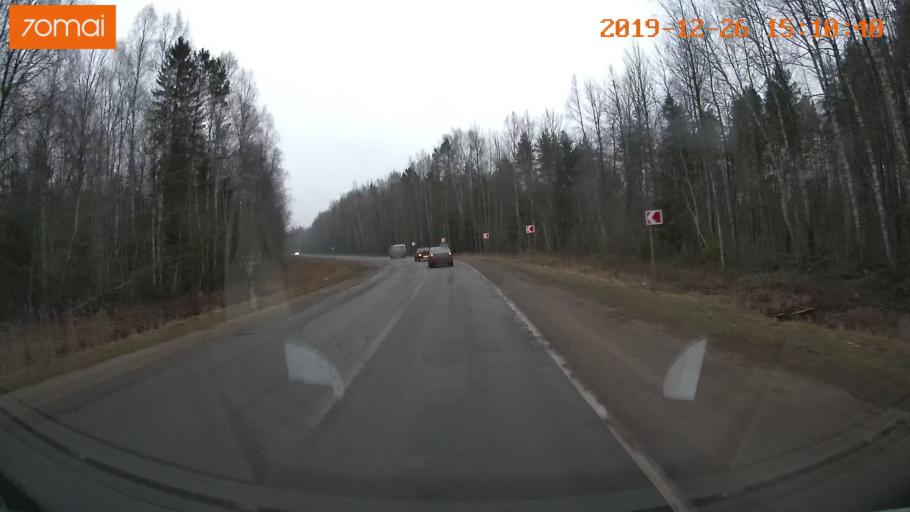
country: RU
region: Jaroslavl
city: Rybinsk
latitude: 58.1389
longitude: 38.8534
